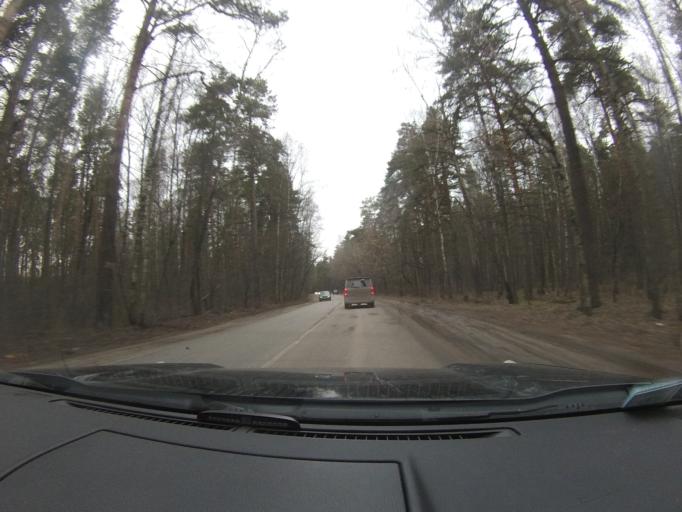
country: RU
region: Moskovskaya
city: Voskresensk
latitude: 55.3349
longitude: 38.6755
